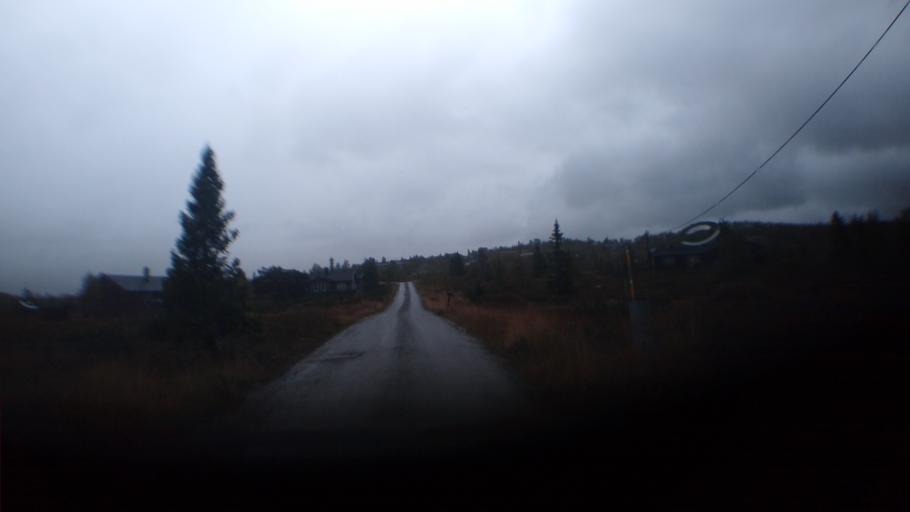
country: NO
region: Oppland
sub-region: Ringebu
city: Ringebu
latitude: 61.6490
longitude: 10.0953
